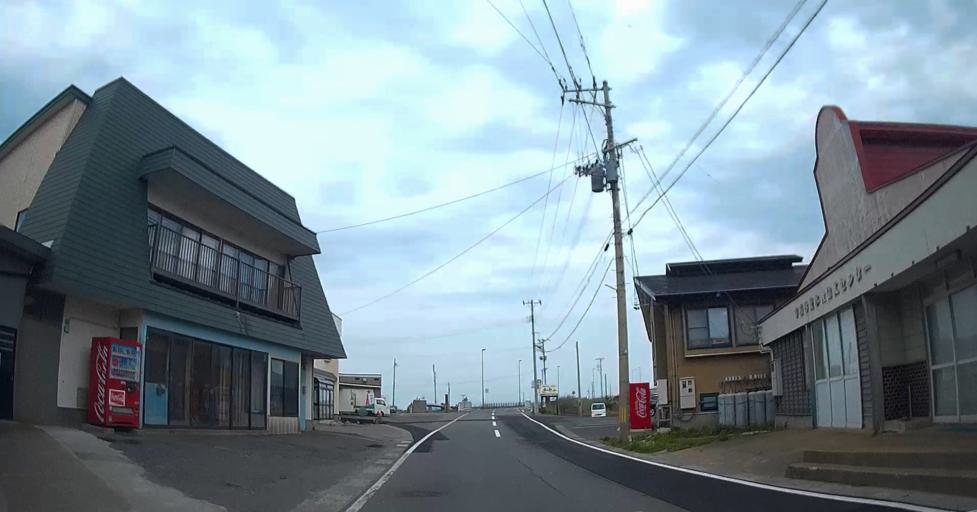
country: JP
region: Aomori
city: Shimokizukuri
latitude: 41.0365
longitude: 140.3293
